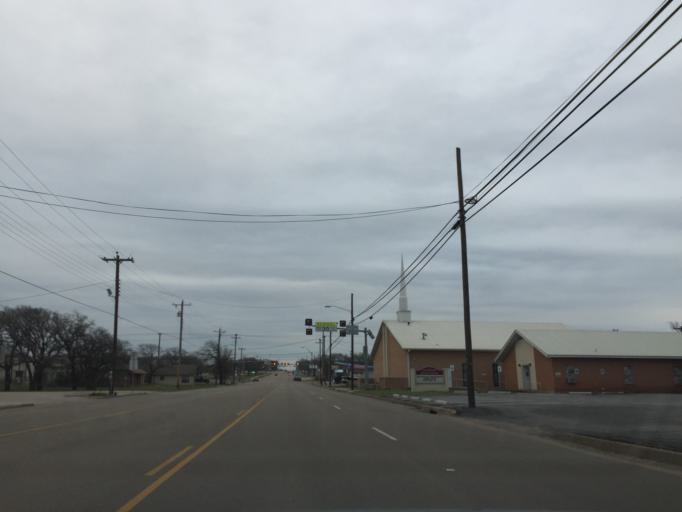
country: US
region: Texas
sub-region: Coryell County
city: Gatesville
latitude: 31.4347
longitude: -97.7271
